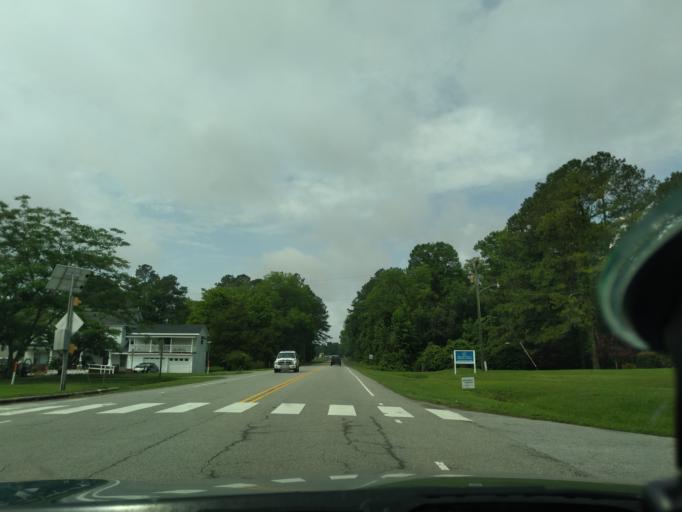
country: US
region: North Carolina
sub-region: Washington County
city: Plymouth
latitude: 35.8787
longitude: -76.6158
